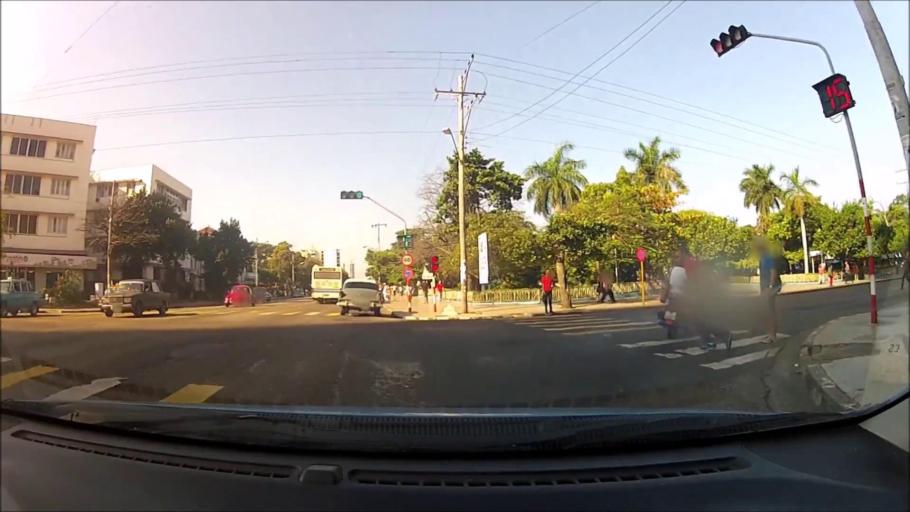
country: CU
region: La Habana
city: Havana
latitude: 23.1400
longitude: -82.3833
